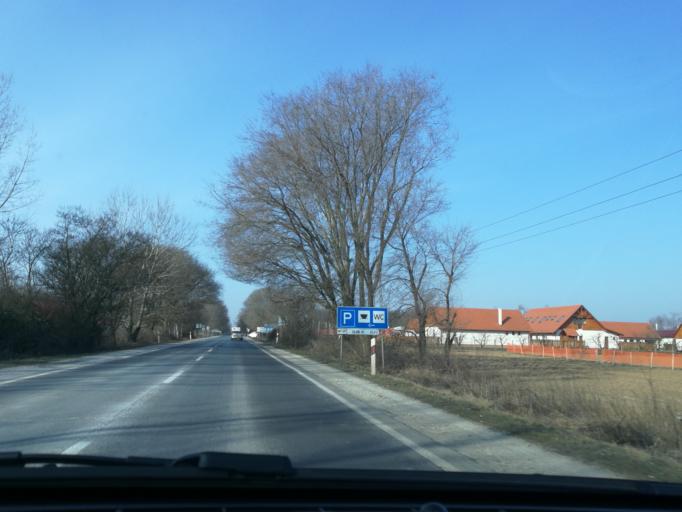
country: HU
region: Szabolcs-Szatmar-Bereg
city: Apagy
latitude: 47.9563
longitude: 21.9200
